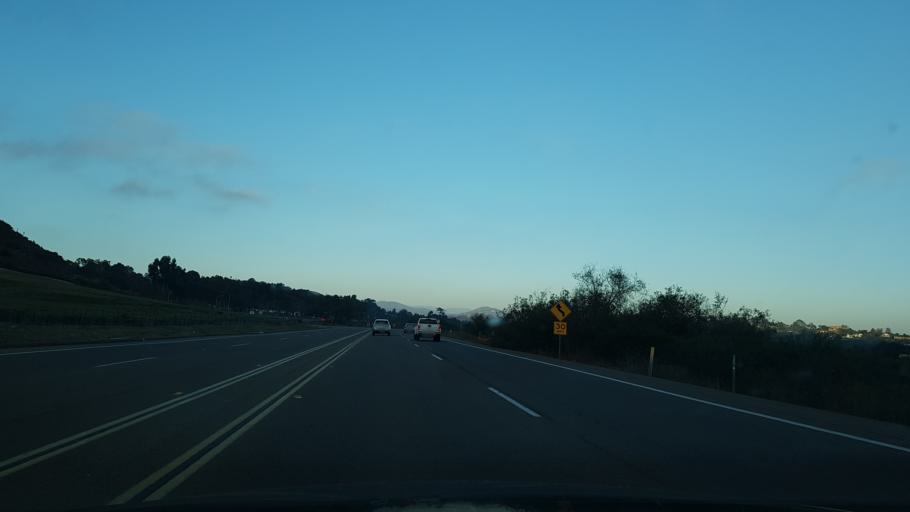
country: US
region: California
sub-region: San Diego County
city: Solana Beach
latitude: 33.0123
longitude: -117.2612
